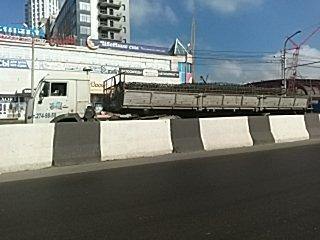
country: RU
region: Krasnoyarskiy
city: Krasnoyarsk
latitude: 56.0346
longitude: 92.9258
